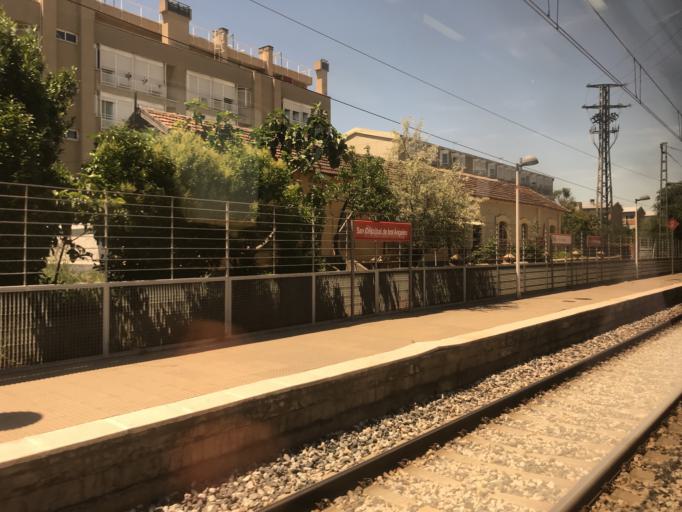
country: ES
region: Madrid
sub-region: Provincia de Madrid
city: Villaverde
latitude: 40.3404
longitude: -3.6838
